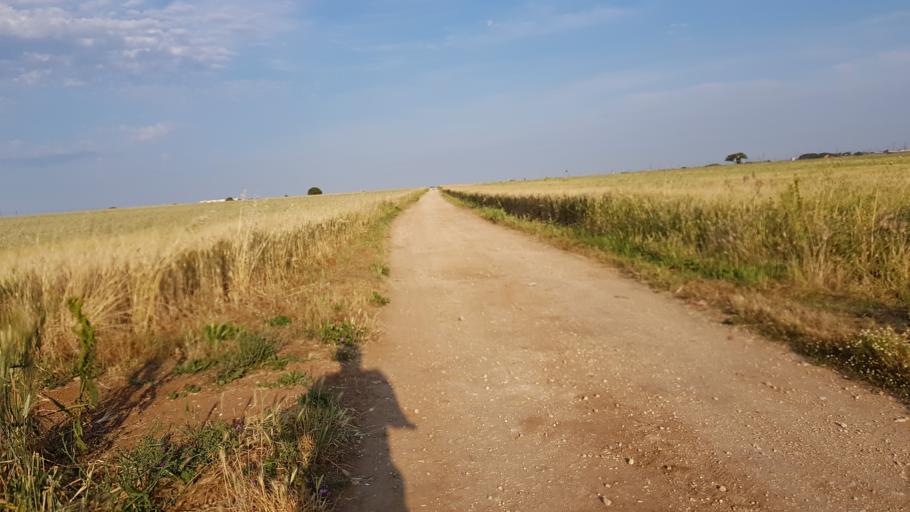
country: IT
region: Apulia
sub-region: Provincia di Brindisi
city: Brindisi
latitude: 40.6264
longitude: 17.8725
